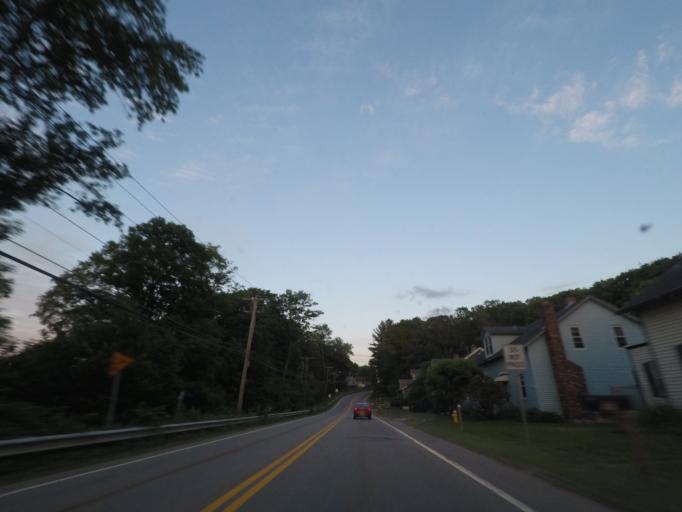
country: US
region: Massachusetts
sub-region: Worcester County
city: Southbridge
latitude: 42.0641
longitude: -72.0077
